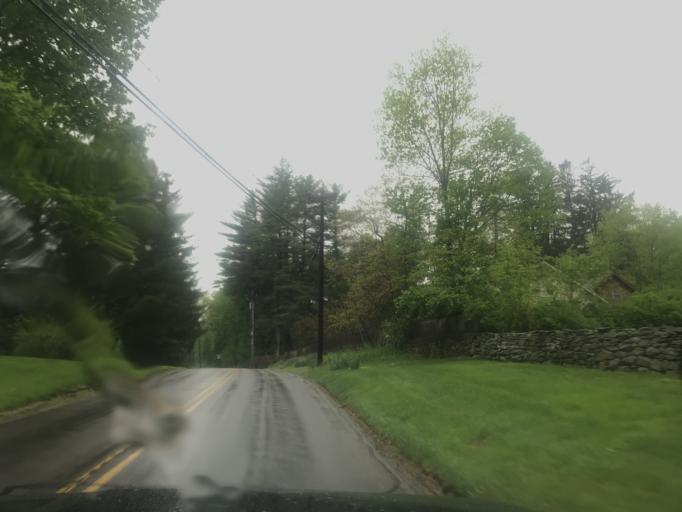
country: US
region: Connecticut
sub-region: Fairfield County
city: Bethel
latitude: 41.3069
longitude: -73.3719
